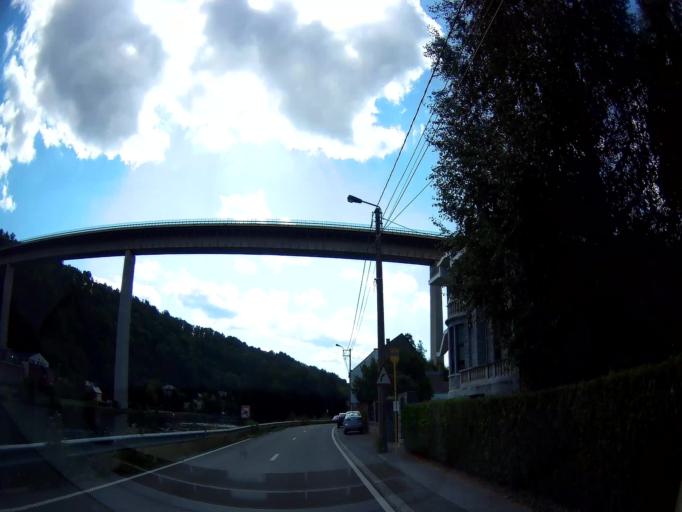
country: BE
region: Wallonia
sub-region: Province de Namur
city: Dinant
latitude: 50.2431
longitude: 4.9190
